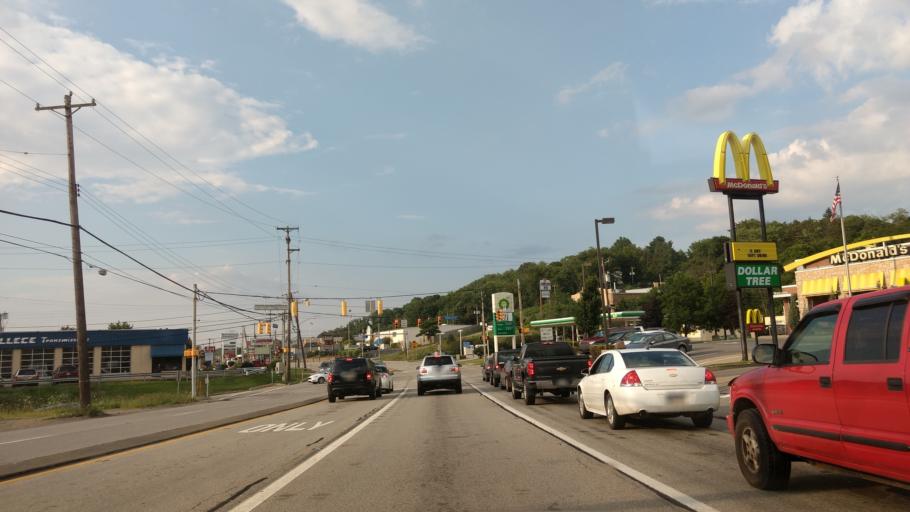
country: US
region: Pennsylvania
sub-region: Allegheny County
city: Allison Park
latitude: 40.5897
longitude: -79.9486
